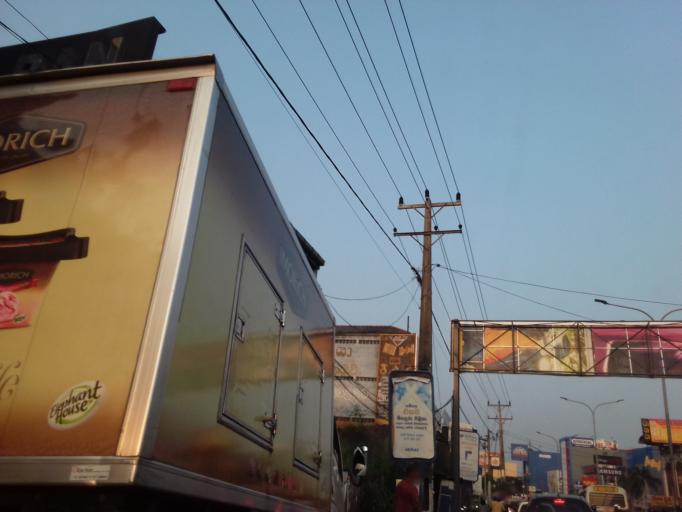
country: LK
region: Western
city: Kelaniya
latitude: 6.9751
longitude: 79.9238
